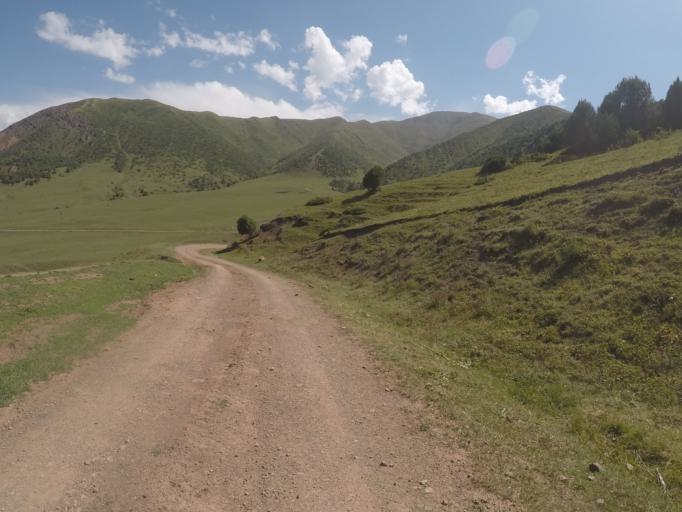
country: KG
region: Chuy
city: Bishkek
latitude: 42.6457
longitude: 74.5694
